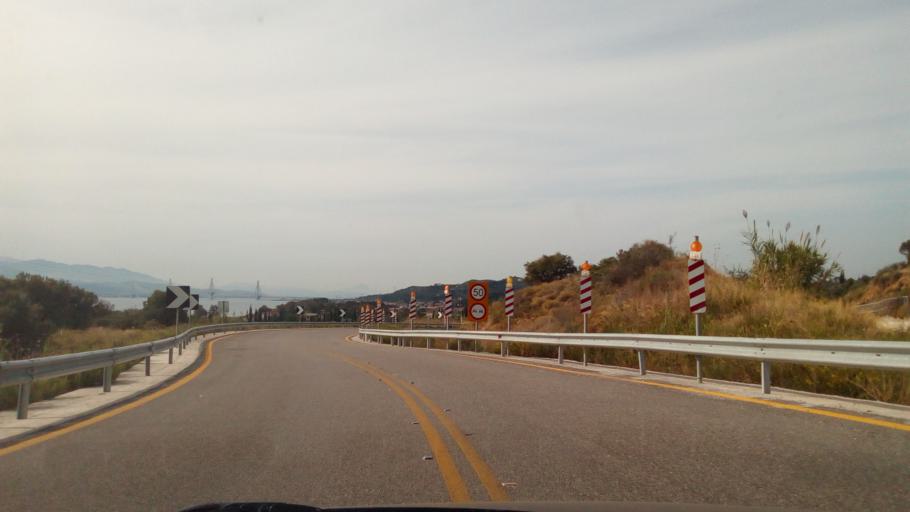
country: GR
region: West Greece
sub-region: Nomos Aitolias kai Akarnanias
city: Nafpaktos
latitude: 38.3775
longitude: 21.7860
